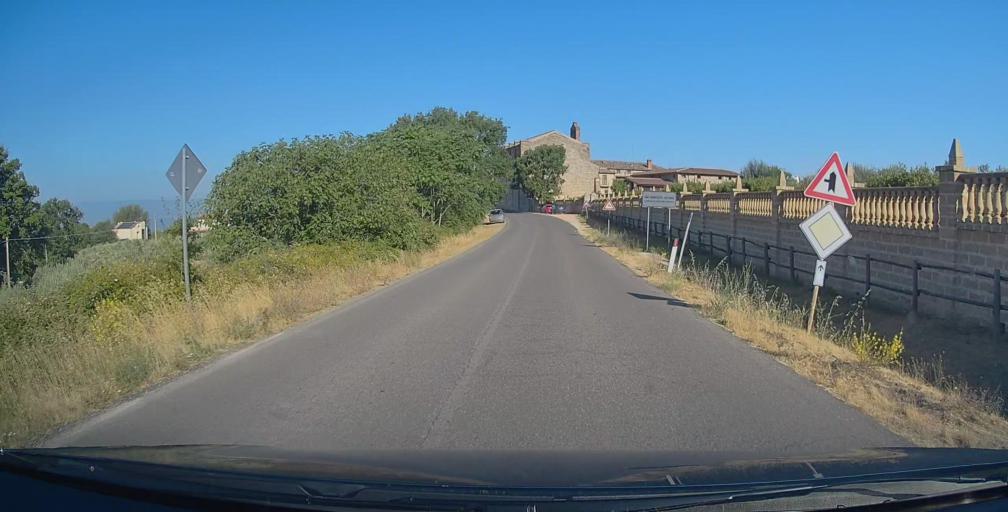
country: IT
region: Umbria
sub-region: Provincia di Terni
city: Calvi dell'Umbria
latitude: 42.4071
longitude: 12.5646
